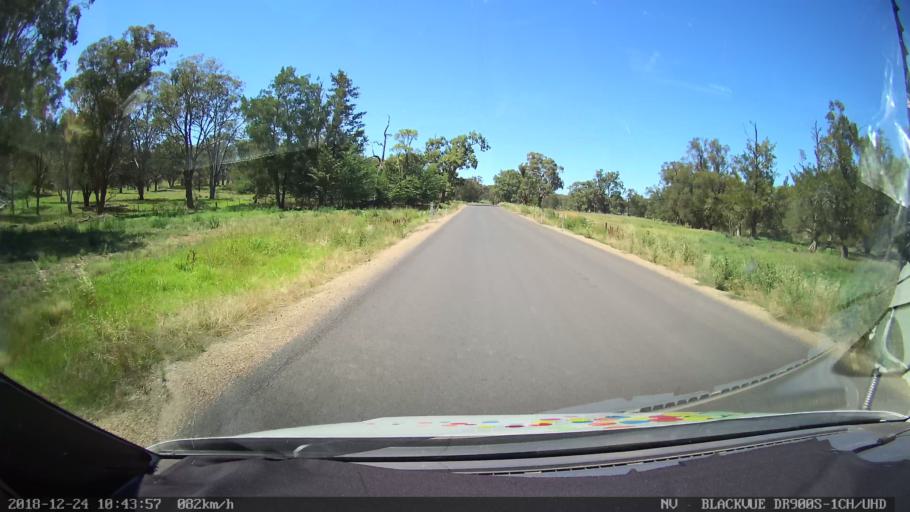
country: AU
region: New South Wales
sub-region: Upper Hunter Shire
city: Merriwa
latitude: -31.8873
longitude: 150.4438
